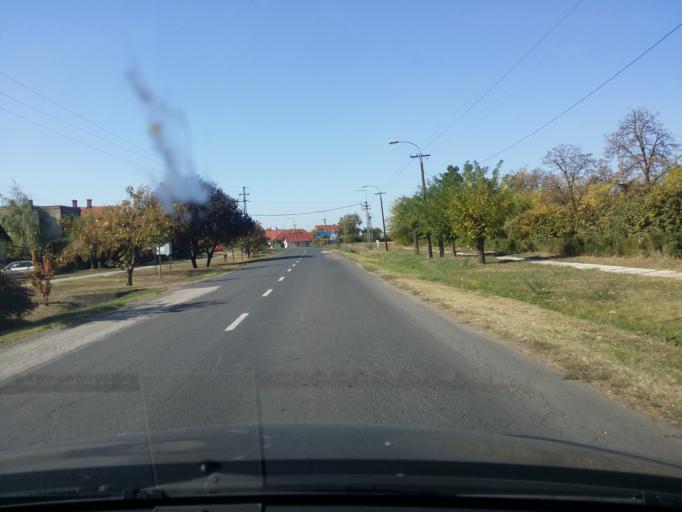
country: HU
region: Jasz-Nagykun-Szolnok
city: Mezotur
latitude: 47.0026
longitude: 20.6016
